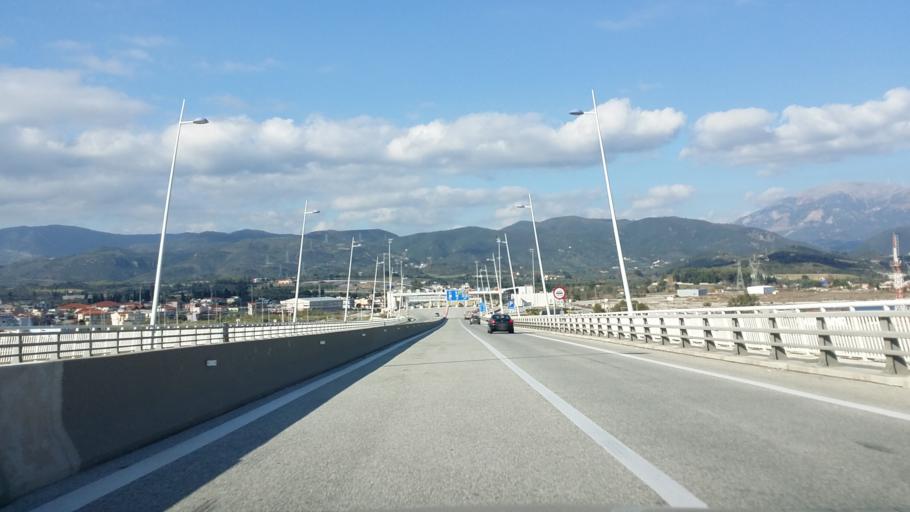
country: GR
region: West Greece
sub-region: Nomos Aitolias kai Akarnanias
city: Antirrio
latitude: 38.3296
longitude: 21.7683
